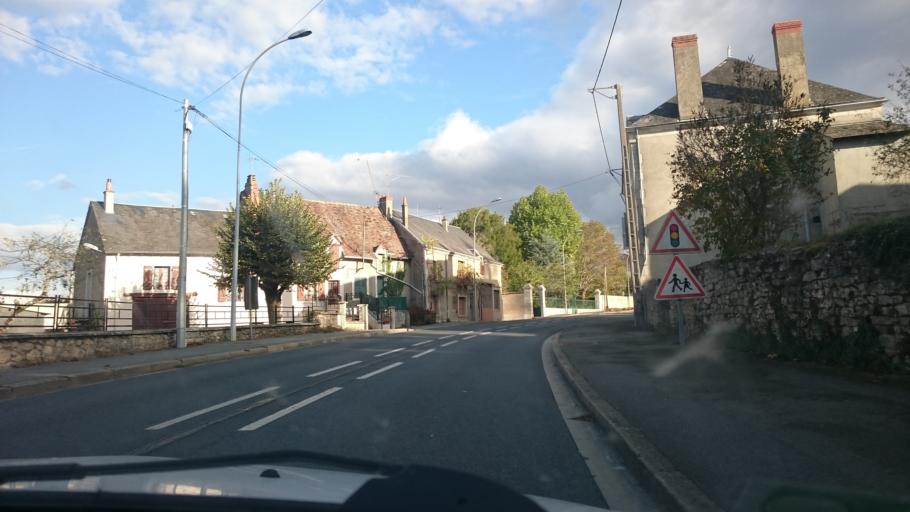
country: FR
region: Centre
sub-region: Departement de l'Indre
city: Saint-Marcel
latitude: 46.6284
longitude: 1.4822
